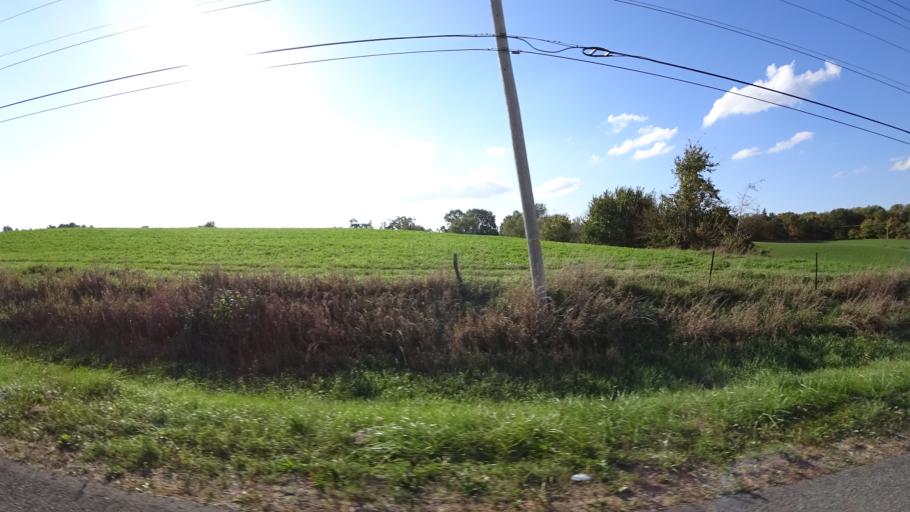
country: US
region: Michigan
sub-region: Saint Joseph County
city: Centreville
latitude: 41.8802
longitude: -85.5068
